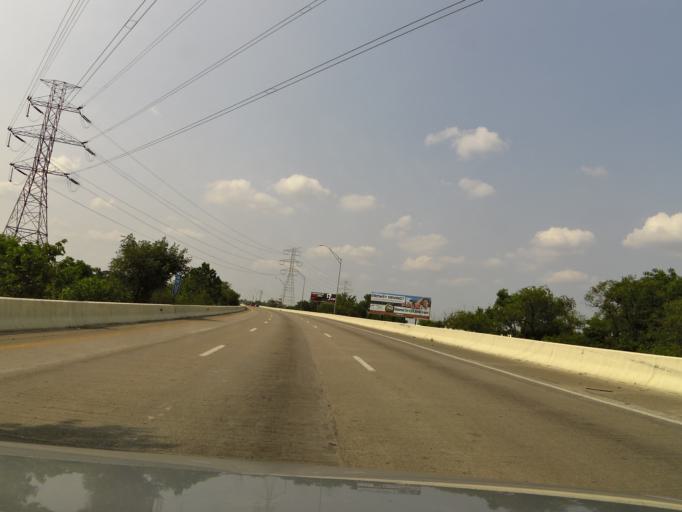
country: US
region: Ohio
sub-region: Hamilton County
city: Reading
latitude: 39.2225
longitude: -84.4481
